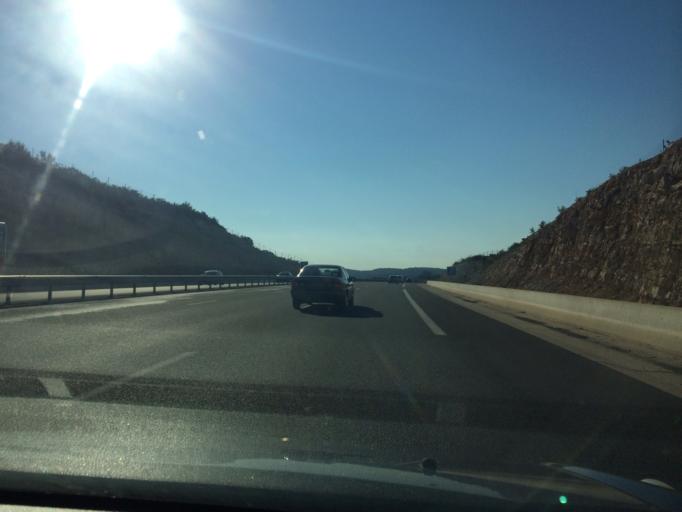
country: FR
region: Languedoc-Roussillon
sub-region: Departement de l'Herault
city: Aniane
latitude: 43.6250
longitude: 3.6179
